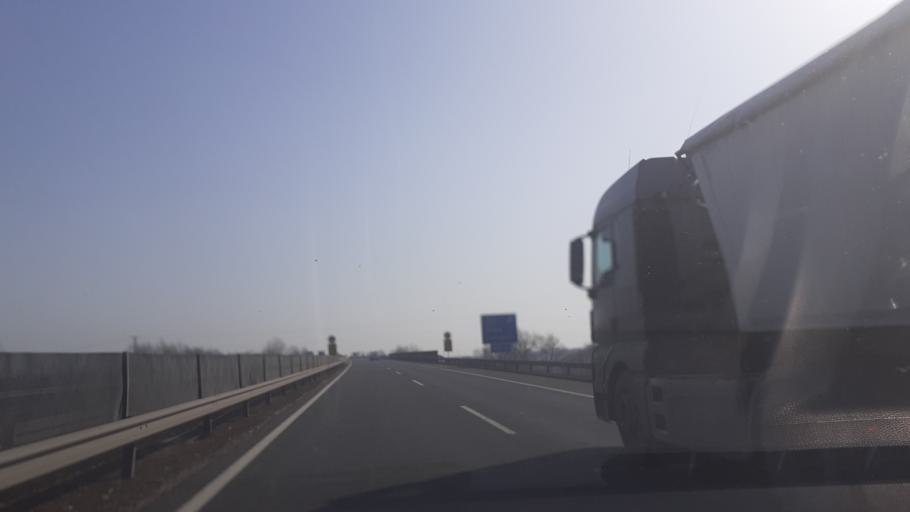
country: HU
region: Bacs-Kiskun
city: Dunavecse
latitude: 46.8988
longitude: 18.9741
